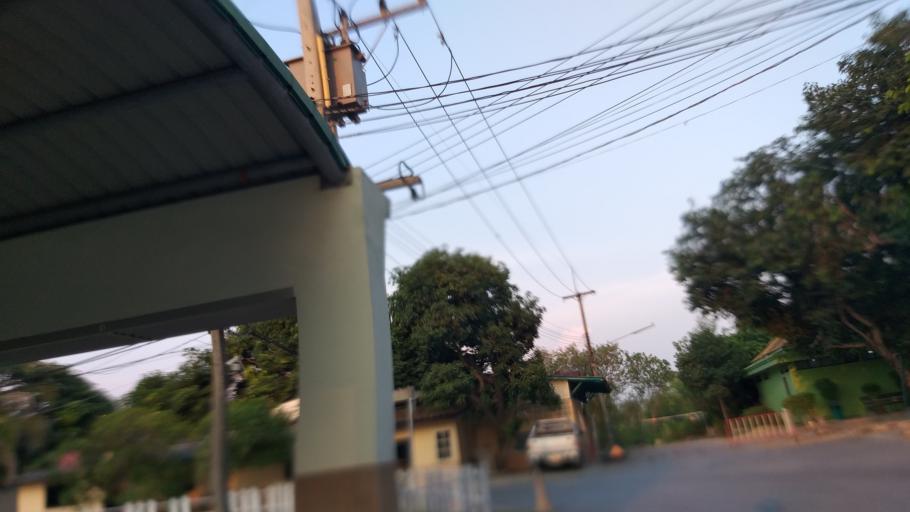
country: TH
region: Pathum Thani
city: Nong Suea
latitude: 14.0691
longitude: 100.8370
